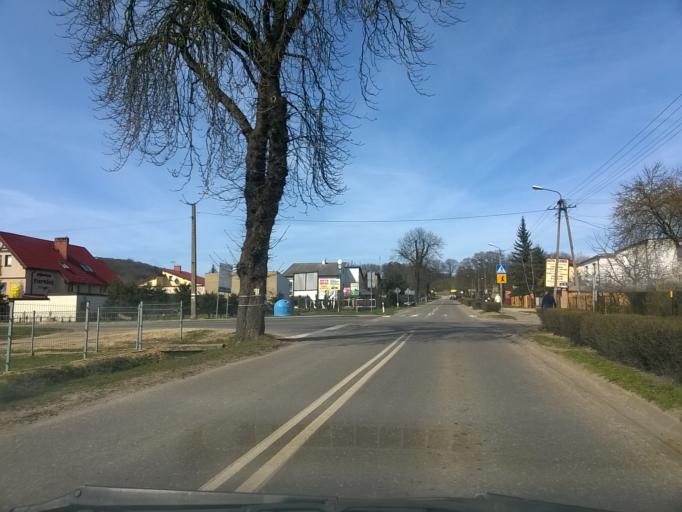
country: PL
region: Greater Poland Voivodeship
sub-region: Powiat pilski
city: Osiek nad Notecia
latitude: 53.1212
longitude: 17.2882
